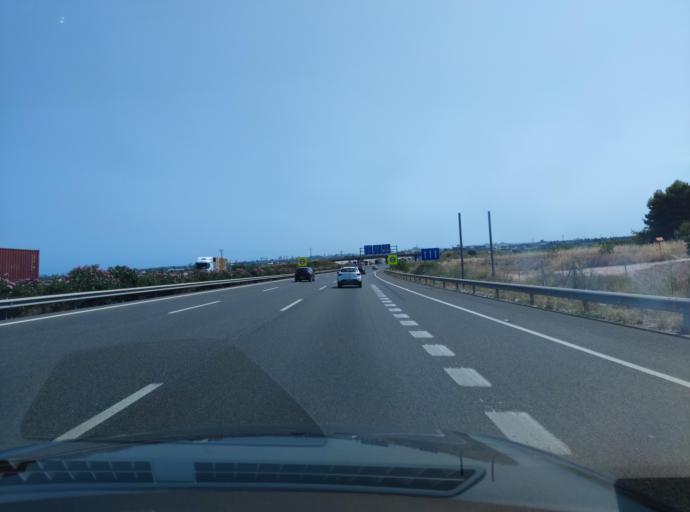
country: ES
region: Valencia
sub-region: Provincia de Valencia
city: Pucol
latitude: 39.6459
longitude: -0.3004
